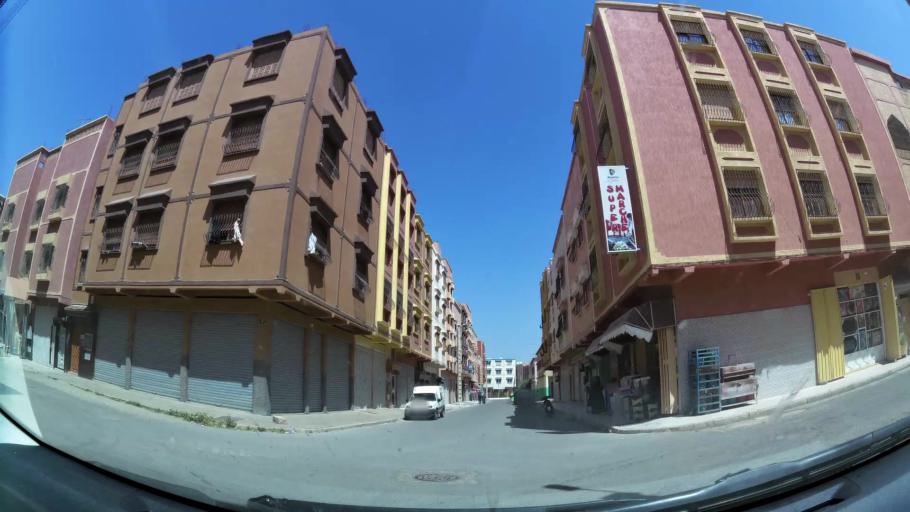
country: MA
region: Souss-Massa-Draa
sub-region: Inezgane-Ait Mellou
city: Inezgane
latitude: 30.3373
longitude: -9.5002
